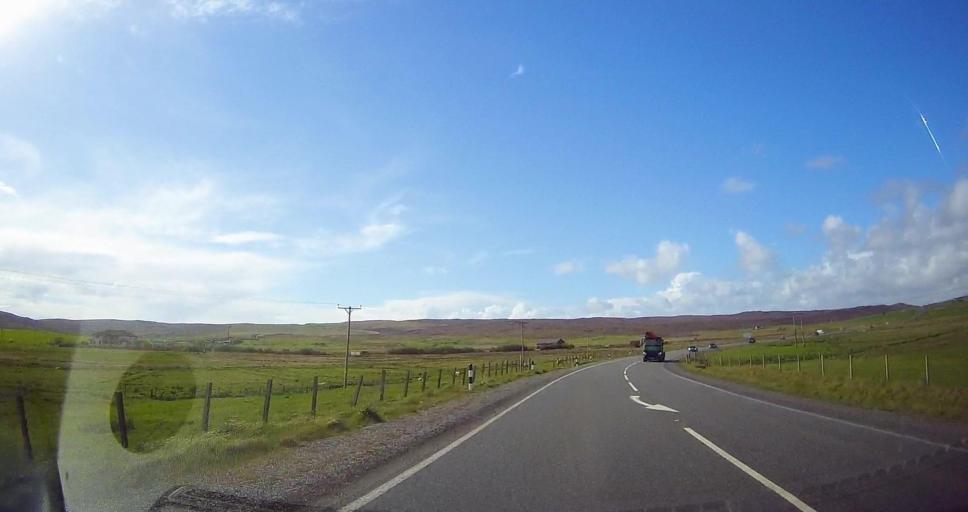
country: GB
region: Scotland
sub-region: Shetland Islands
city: Lerwick
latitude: 60.1875
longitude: -1.2287
